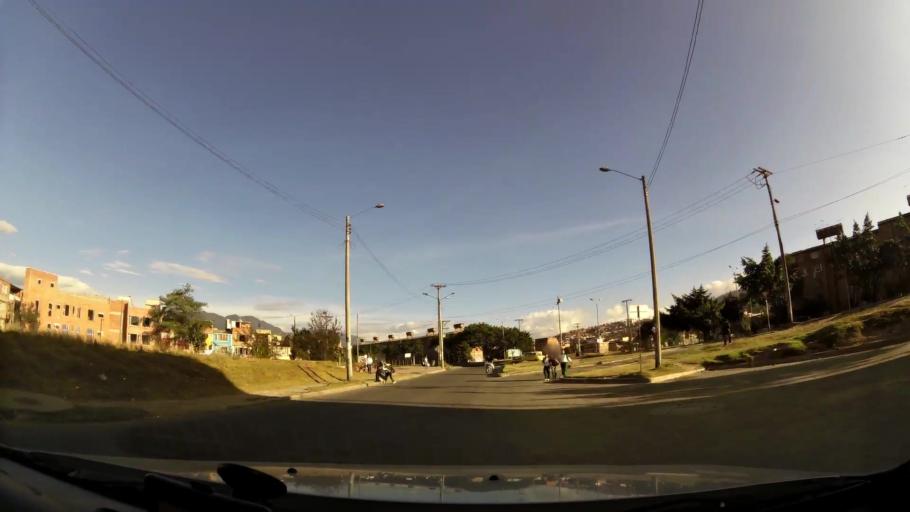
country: CO
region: Cundinamarca
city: Soacha
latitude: 4.5705
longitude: -74.1479
